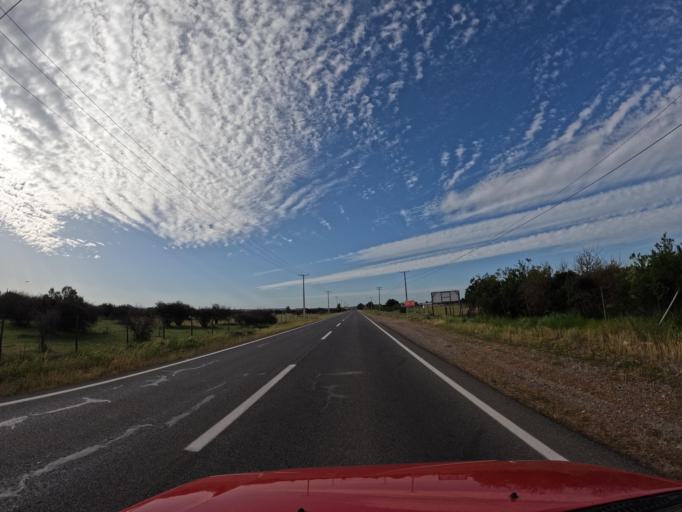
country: CL
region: Valparaiso
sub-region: San Antonio Province
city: San Antonio
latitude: -34.1601
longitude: -71.7320
